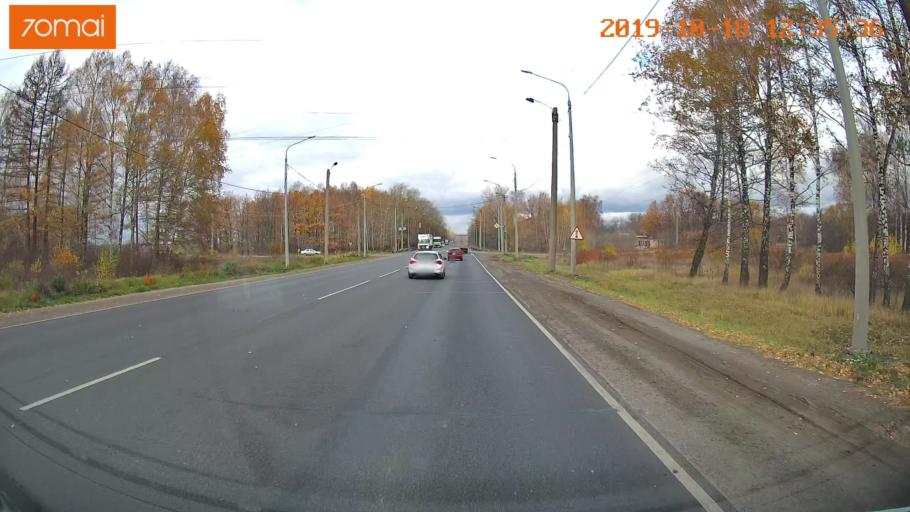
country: RU
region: Rjazan
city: Ryazan'
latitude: 54.6262
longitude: 39.6354
